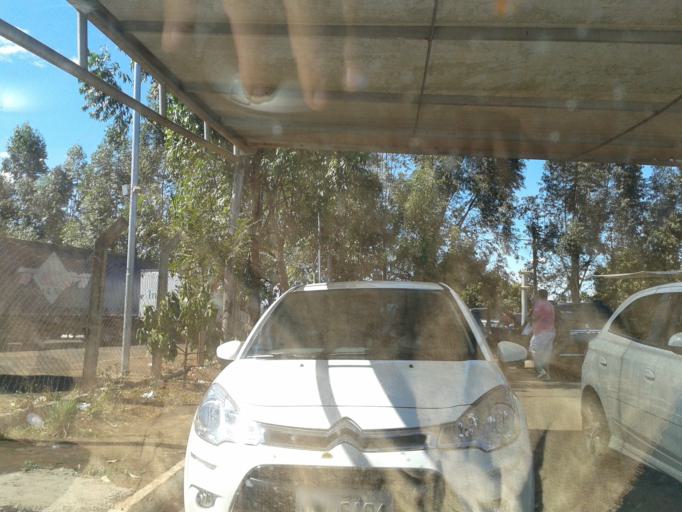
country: BR
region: Goias
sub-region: Itumbiara
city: Itumbiara
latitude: -18.4247
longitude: -49.1926
